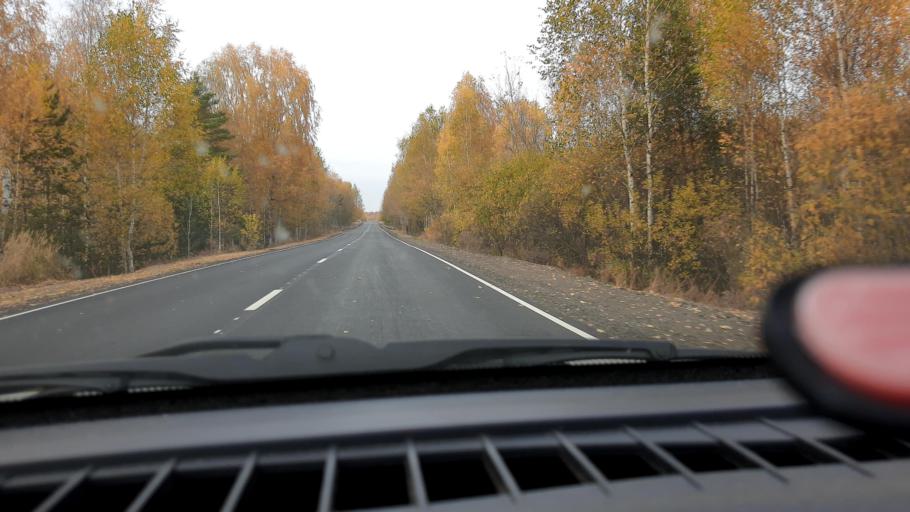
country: RU
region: Nizjnij Novgorod
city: Novaya Balakhna
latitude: 56.5659
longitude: 43.7195
